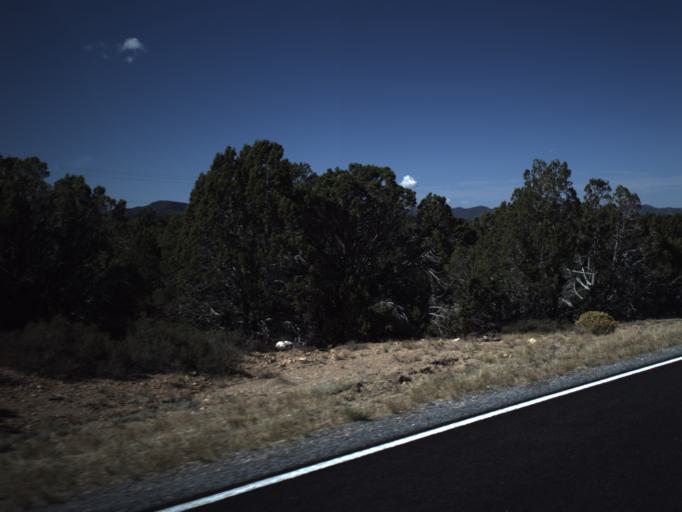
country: US
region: Utah
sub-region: Iron County
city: Cedar City
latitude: 37.6095
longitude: -113.3694
